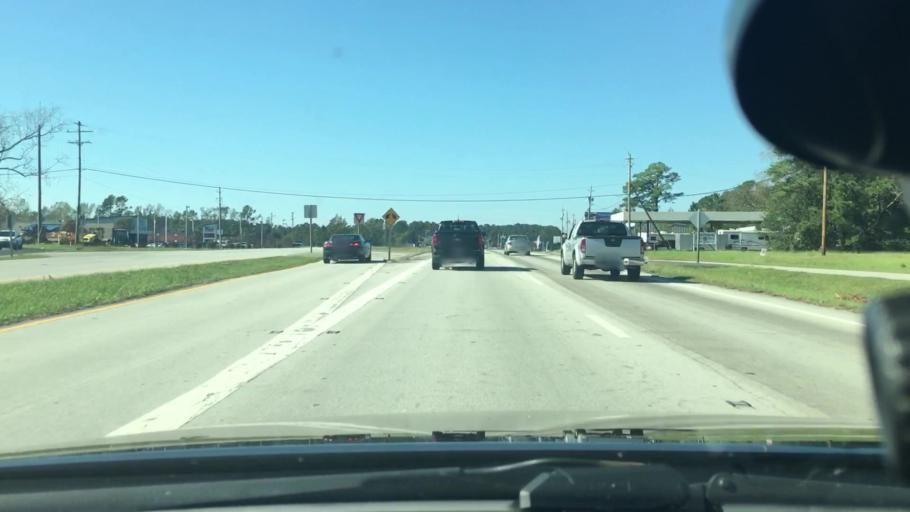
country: US
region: North Carolina
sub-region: Craven County
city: Havelock
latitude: 34.8928
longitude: -76.9243
